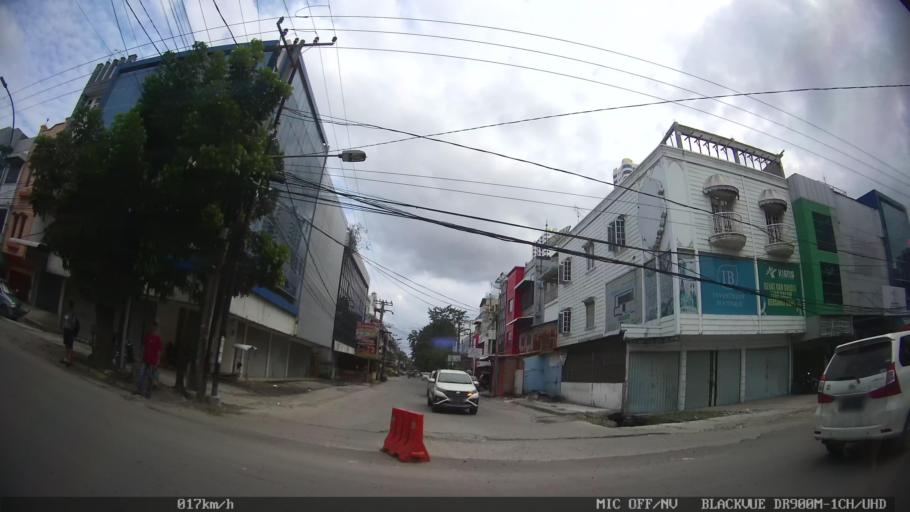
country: ID
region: North Sumatra
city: Medan
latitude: 3.5945
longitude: 98.6816
